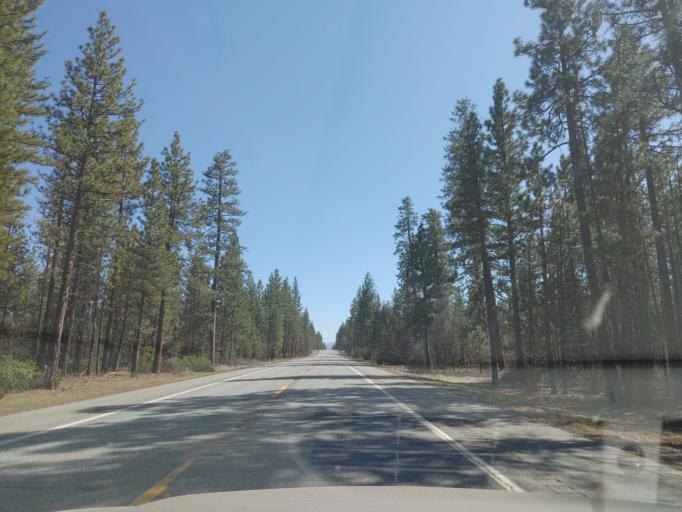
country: US
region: California
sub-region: Shasta County
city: Burney
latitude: 40.9740
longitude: -121.6206
